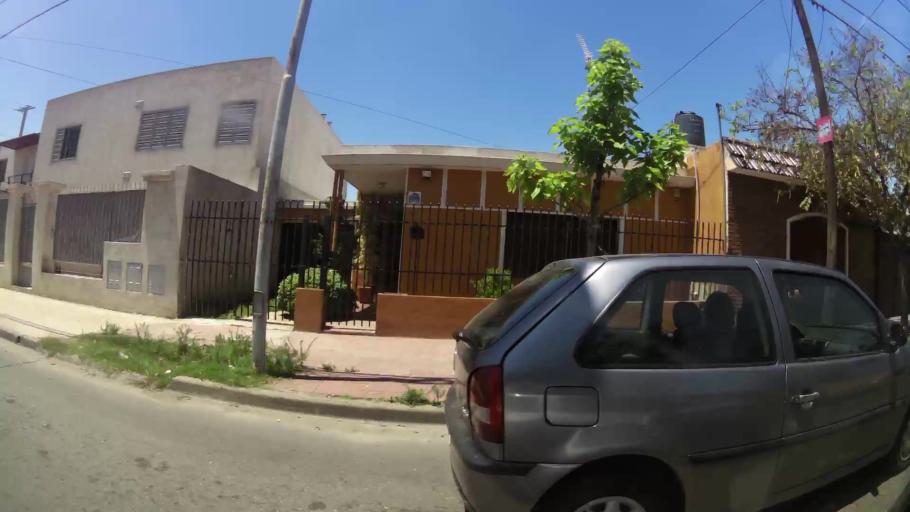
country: AR
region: Cordoba
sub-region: Departamento de Capital
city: Cordoba
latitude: -31.4017
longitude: -64.2164
